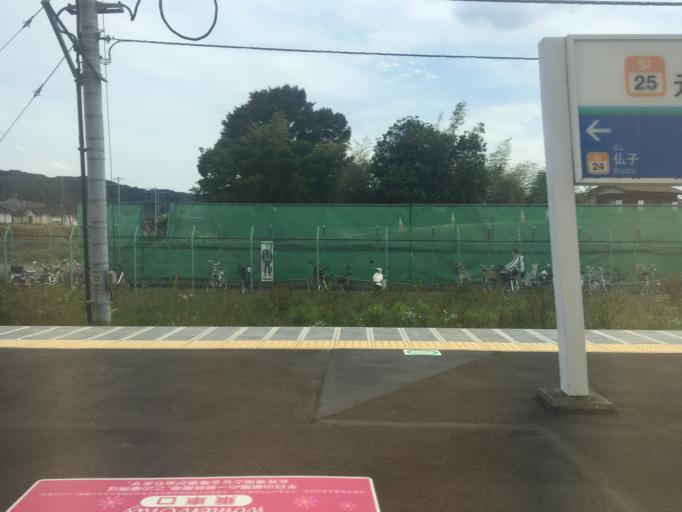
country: JP
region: Saitama
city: Hanno
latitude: 35.8408
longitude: 139.3447
